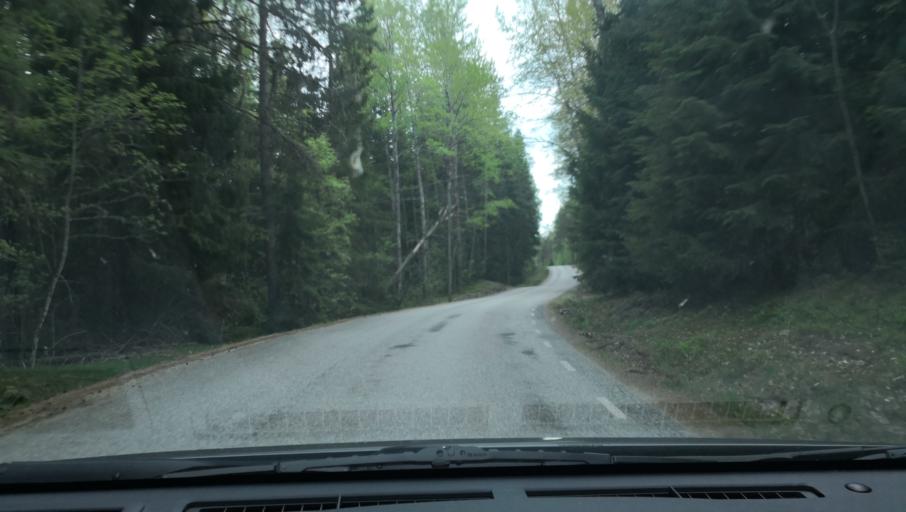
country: SE
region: Vaestmanland
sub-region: Skinnskattebergs Kommun
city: Skinnskatteberg
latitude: 59.8267
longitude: 15.5534
